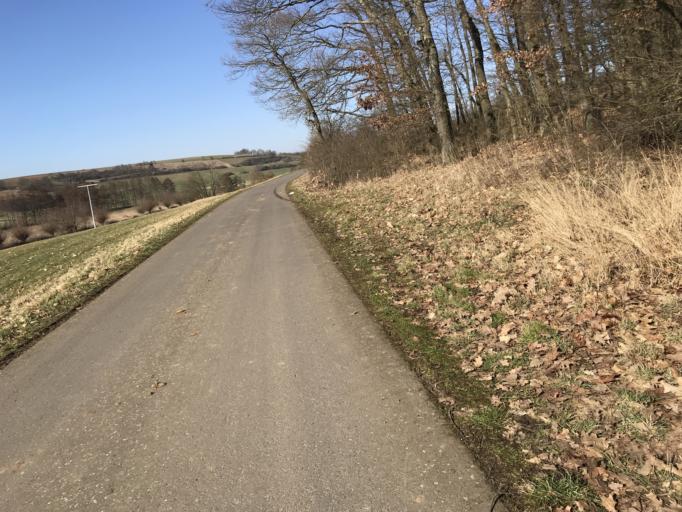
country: DE
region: Hesse
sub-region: Regierungsbezirk Darmstadt
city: Nidda
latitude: 50.3885
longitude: 8.9794
